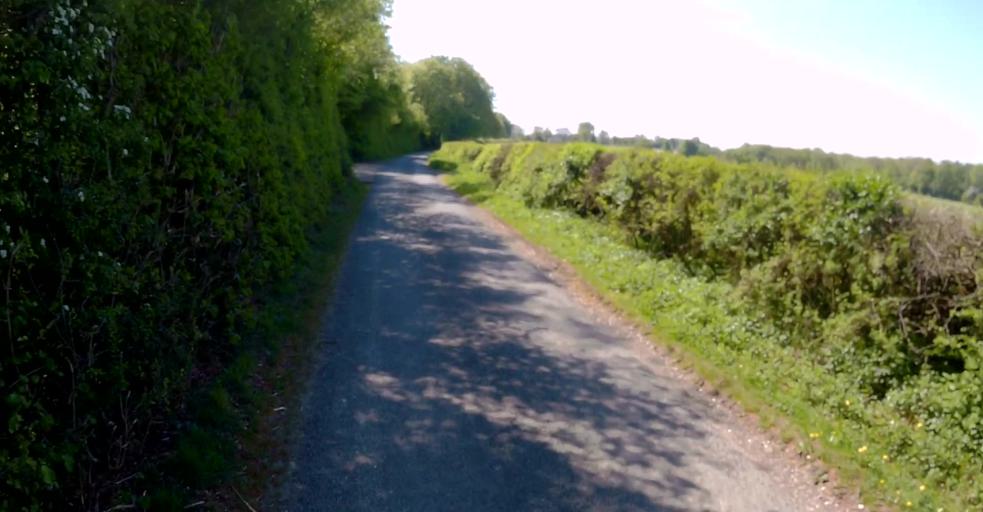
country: GB
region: England
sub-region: Hampshire
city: Overton
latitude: 51.1977
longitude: -1.2434
